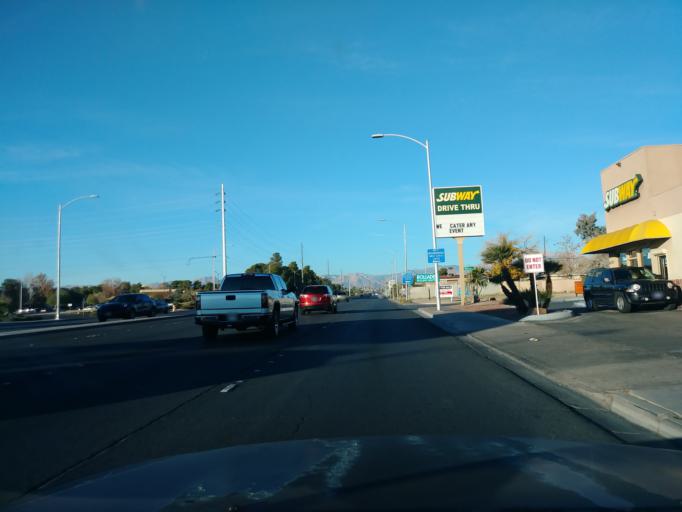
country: US
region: Nevada
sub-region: Clark County
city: Spring Valley
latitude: 36.1593
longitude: -115.2251
